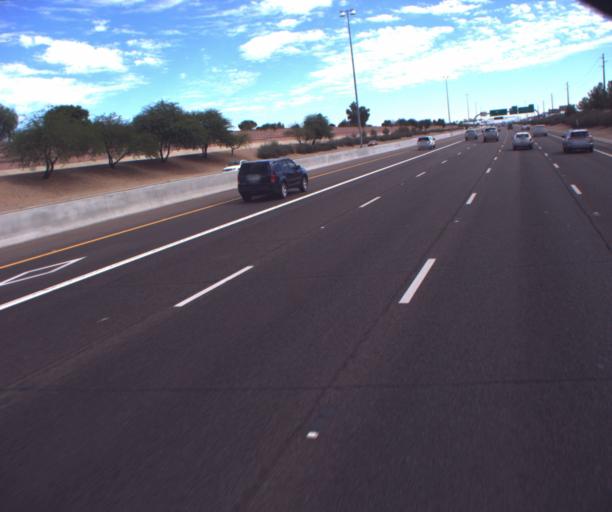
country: US
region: Arizona
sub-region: Maricopa County
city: Guadalupe
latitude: 33.2912
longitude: -111.9341
